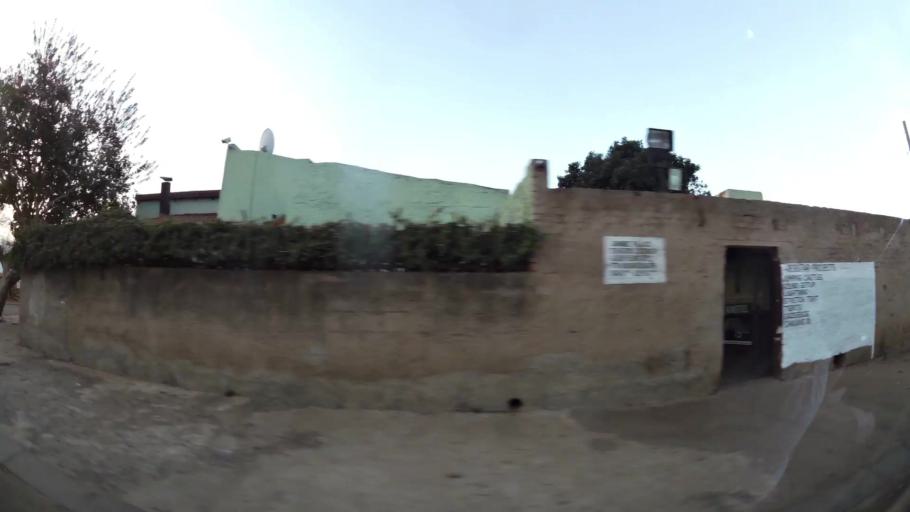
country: ZA
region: Gauteng
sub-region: West Rand District Municipality
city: Randfontein
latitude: -26.2030
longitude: 27.7135
